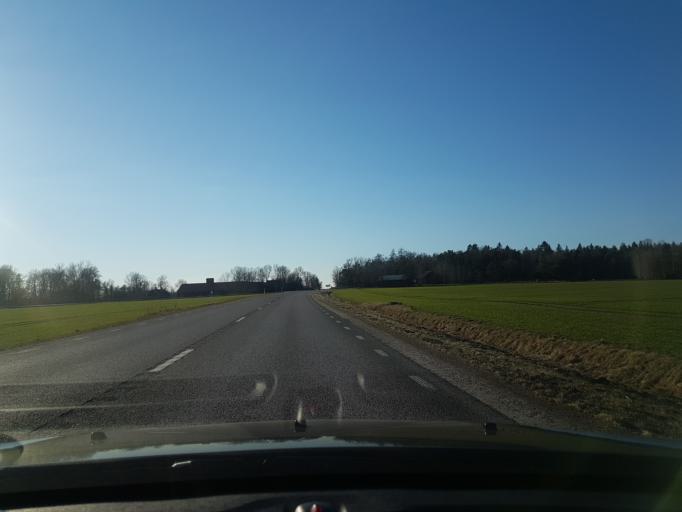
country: SE
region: Uppsala
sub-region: Enkopings Kommun
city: Orsundsbro
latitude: 59.8737
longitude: 17.2959
